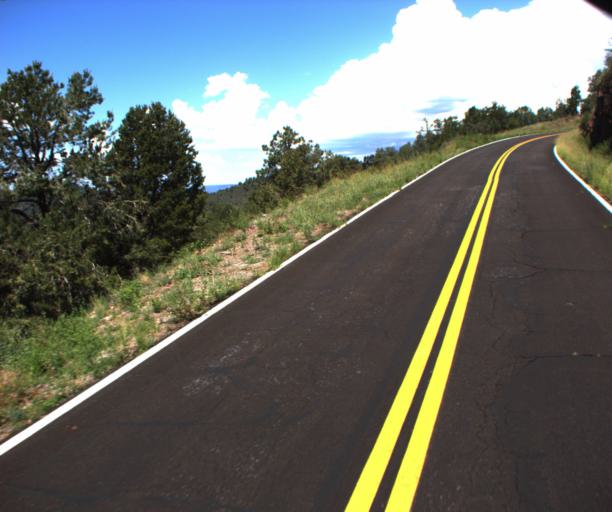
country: US
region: Arizona
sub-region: Greenlee County
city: Morenci
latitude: 33.4322
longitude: -109.3768
